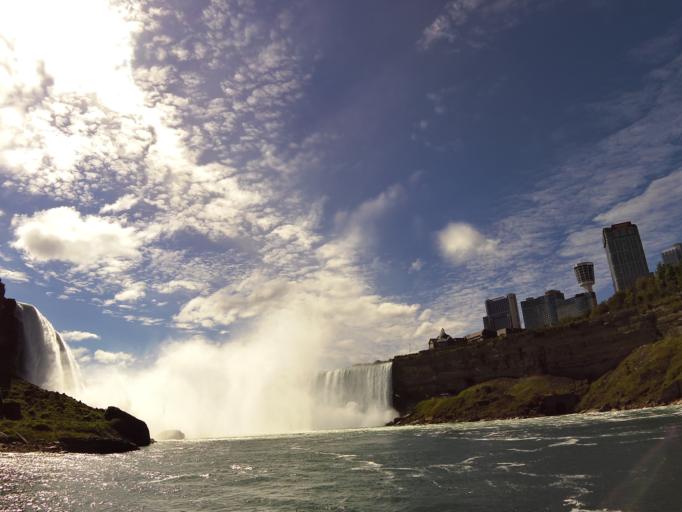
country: CA
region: Ontario
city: Niagara Falls
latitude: 43.0820
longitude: -79.0747
